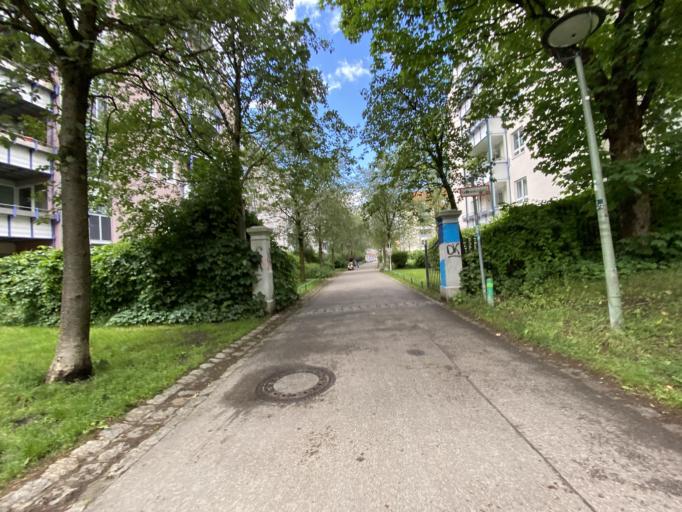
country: DE
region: Bavaria
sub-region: Upper Bavaria
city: Munich
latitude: 48.1362
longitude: 11.5174
